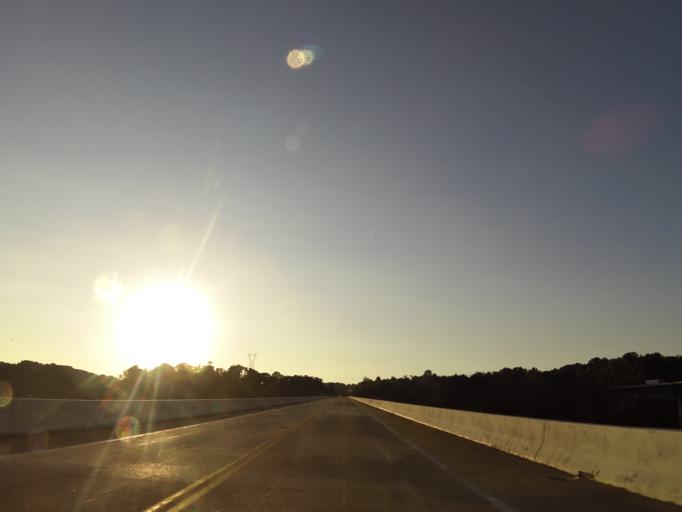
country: US
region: Tennessee
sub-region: Jefferson County
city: Dandridge
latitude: 36.0390
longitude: -83.3372
